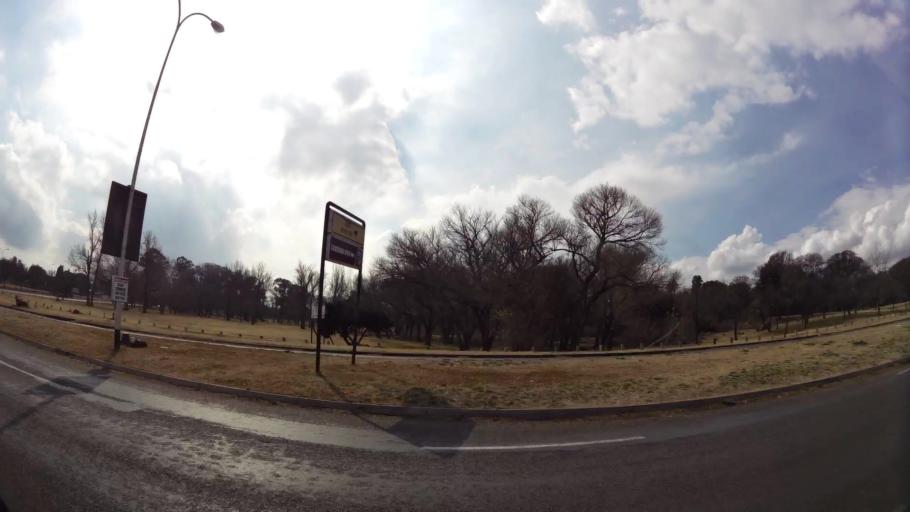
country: ZA
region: Gauteng
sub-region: Sedibeng District Municipality
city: Vanderbijlpark
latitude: -26.7330
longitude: 27.8383
